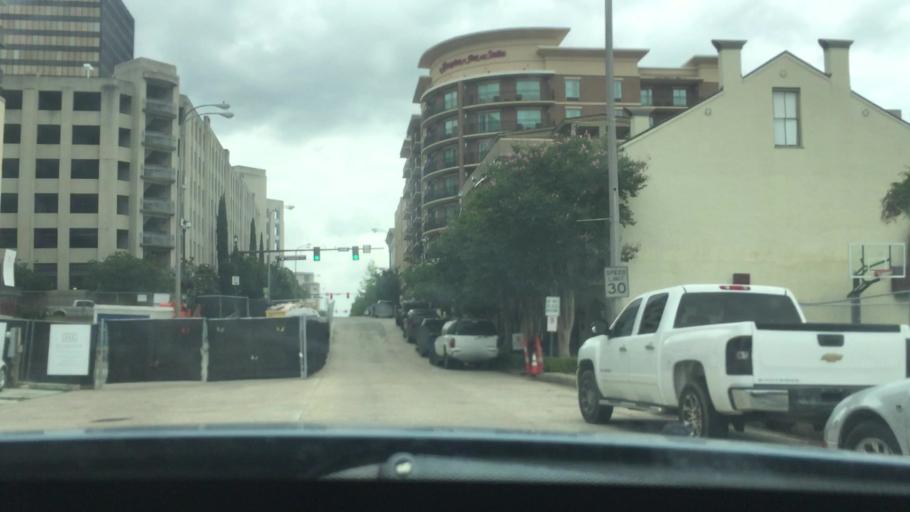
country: US
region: Louisiana
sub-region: West Baton Rouge Parish
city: Port Allen
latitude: 30.4514
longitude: -91.1904
